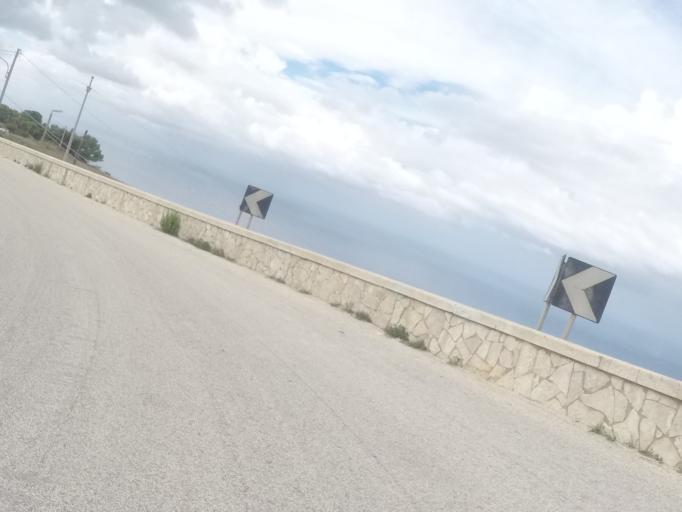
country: IT
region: Sicily
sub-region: Trapani
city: Erice
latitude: 38.0487
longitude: 12.5811
